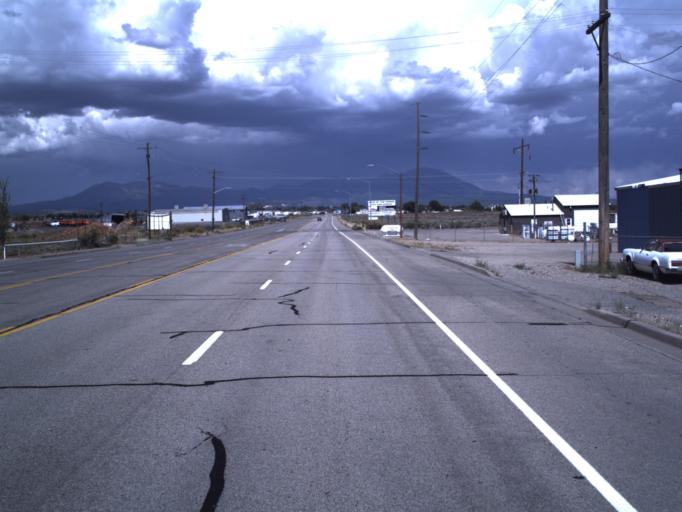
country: US
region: Utah
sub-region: San Juan County
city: Blanding
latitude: 37.5978
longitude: -109.4785
